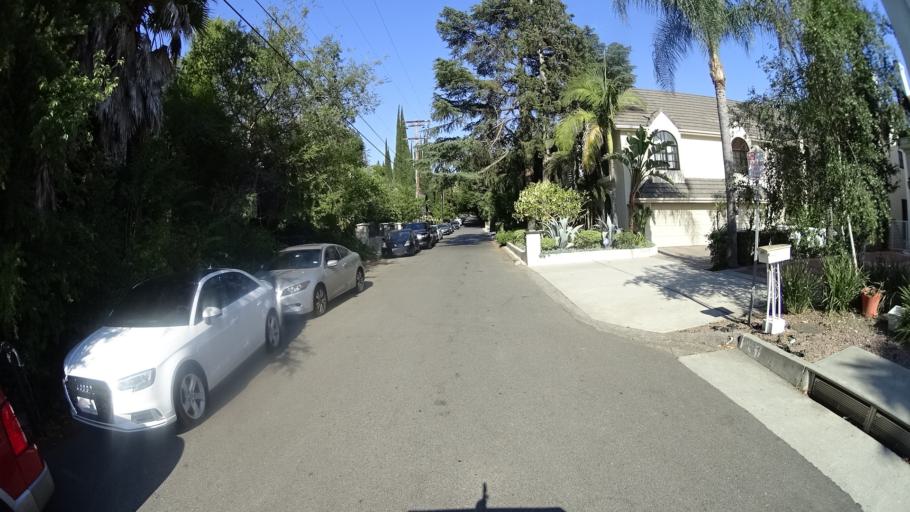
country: US
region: California
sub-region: Los Angeles County
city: Universal City
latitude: 34.1331
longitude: -118.3857
